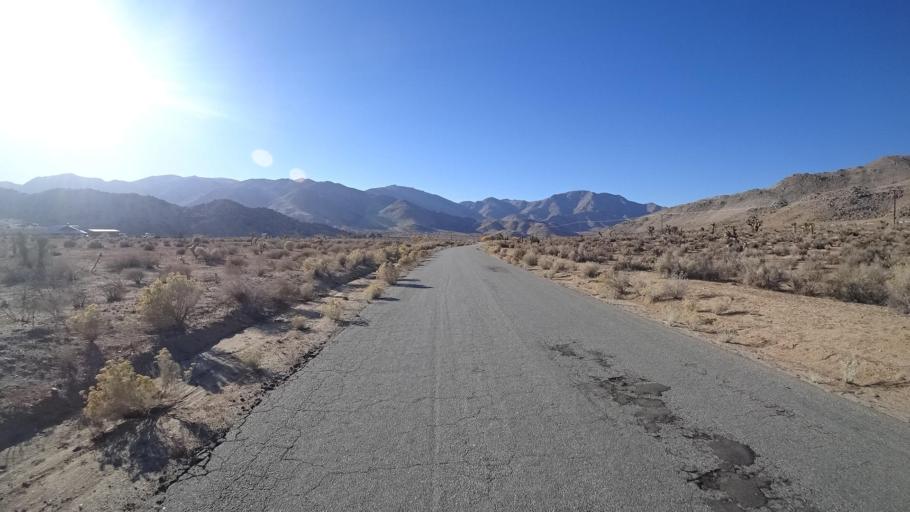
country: US
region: California
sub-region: Kern County
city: Weldon
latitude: 35.5567
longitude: -118.2244
